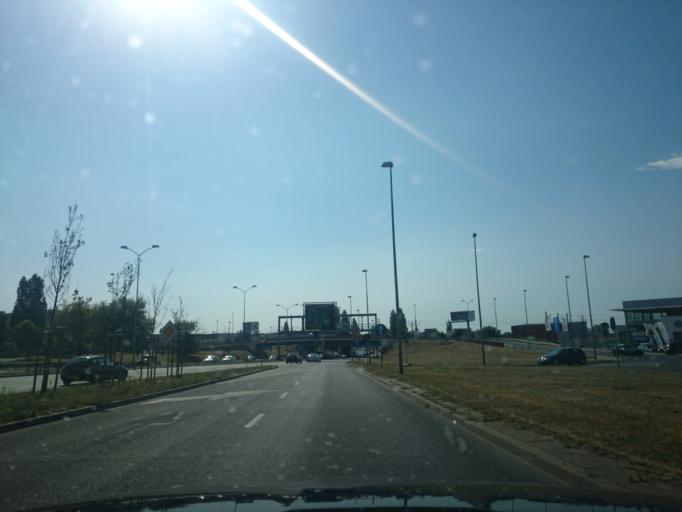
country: PL
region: West Pomeranian Voivodeship
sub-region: Szczecin
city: Szczecin
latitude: 53.3845
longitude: 14.6521
